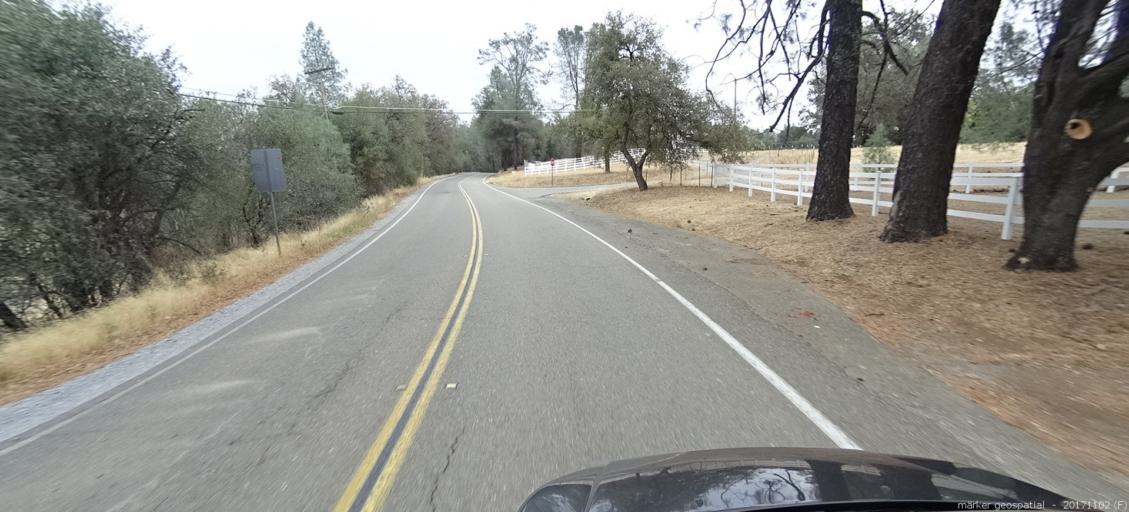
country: US
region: California
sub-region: Shasta County
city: Shasta Lake
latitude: 40.6786
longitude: -122.3010
